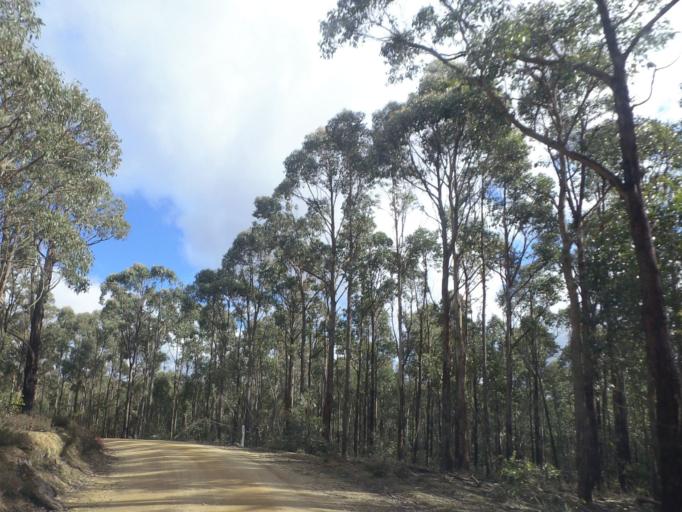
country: AU
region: Victoria
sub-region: Moorabool
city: Bacchus Marsh
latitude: -37.4596
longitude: 144.4414
